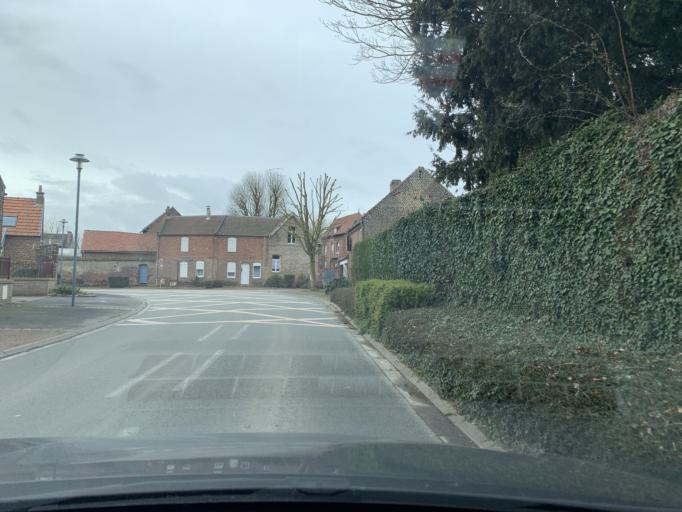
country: FR
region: Nord-Pas-de-Calais
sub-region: Departement du Nord
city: Escaudoeuvres
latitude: 50.1583
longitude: 3.2802
